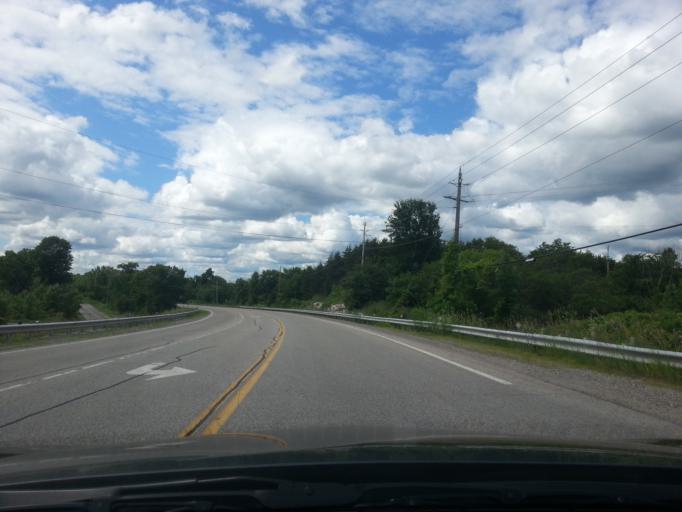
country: CA
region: Ontario
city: Perth
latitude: 44.7157
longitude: -76.1737
